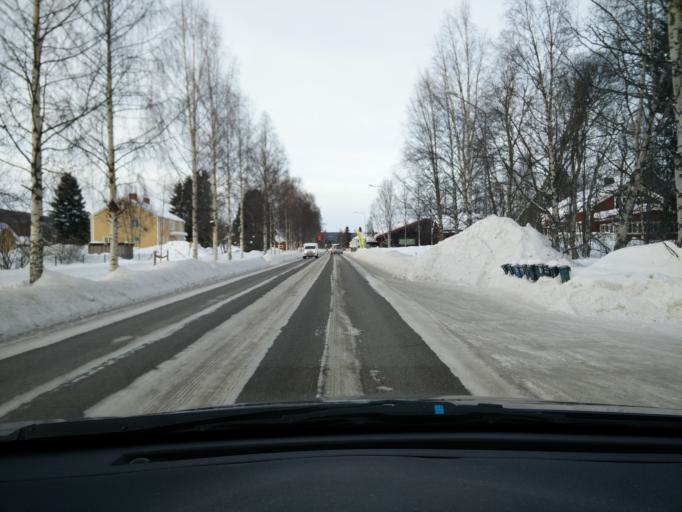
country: SE
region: Jaemtland
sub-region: Harjedalens Kommun
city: Sveg
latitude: 62.4465
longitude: 13.8626
